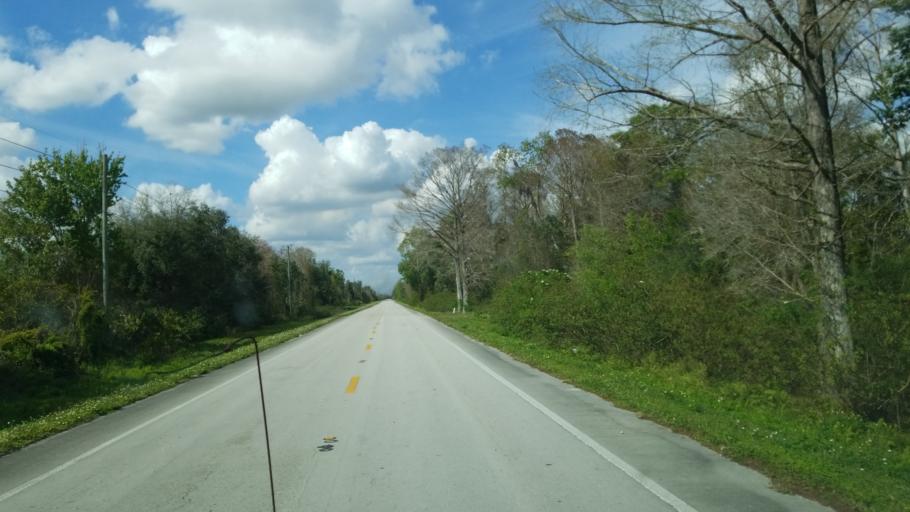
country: US
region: Florida
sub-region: Brevard County
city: June Park
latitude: 28.0074
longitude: -81.0250
